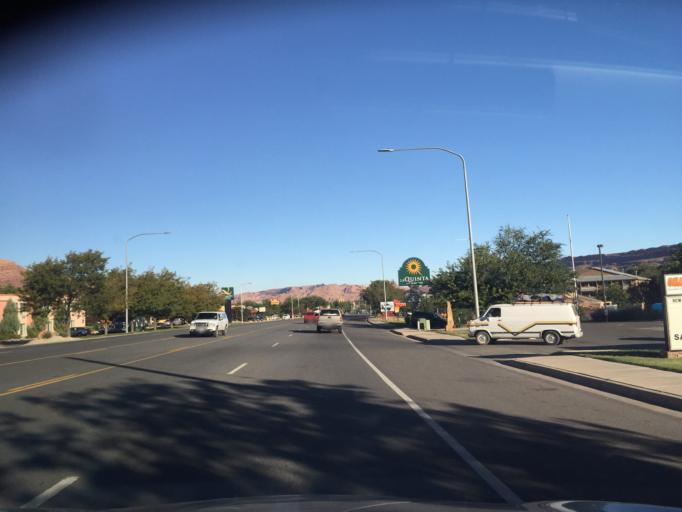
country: US
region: Utah
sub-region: Grand County
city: Moab
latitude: 38.5607
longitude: -109.5472
